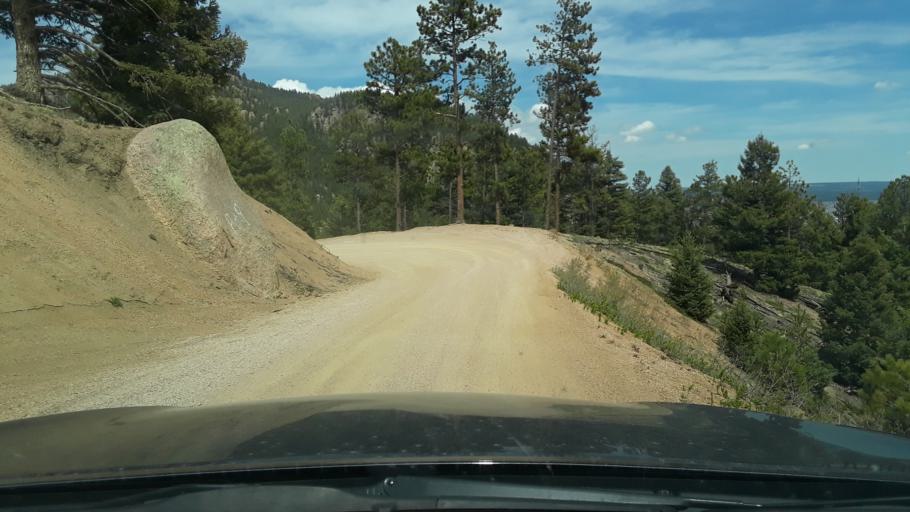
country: US
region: Colorado
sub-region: El Paso County
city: Palmer Lake
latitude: 39.0681
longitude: -104.9375
